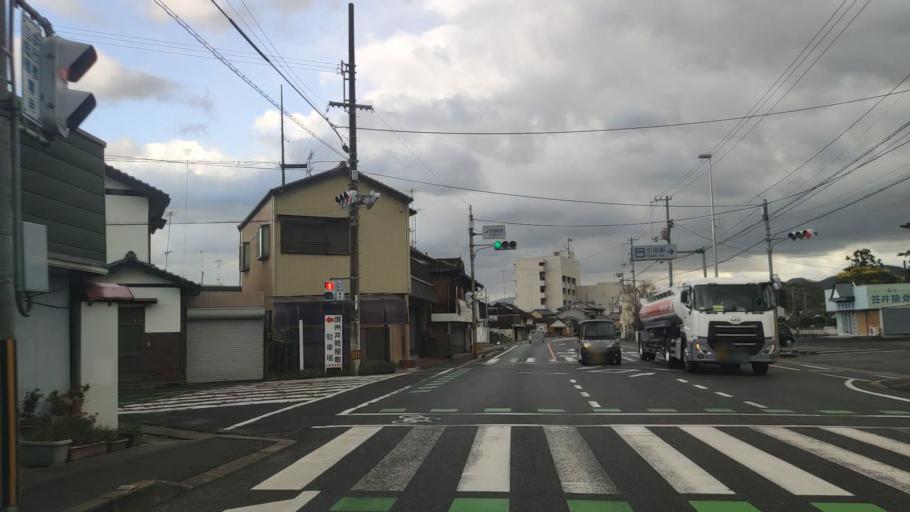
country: JP
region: Tokushima
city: Ishii
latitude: 34.2249
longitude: 134.4018
